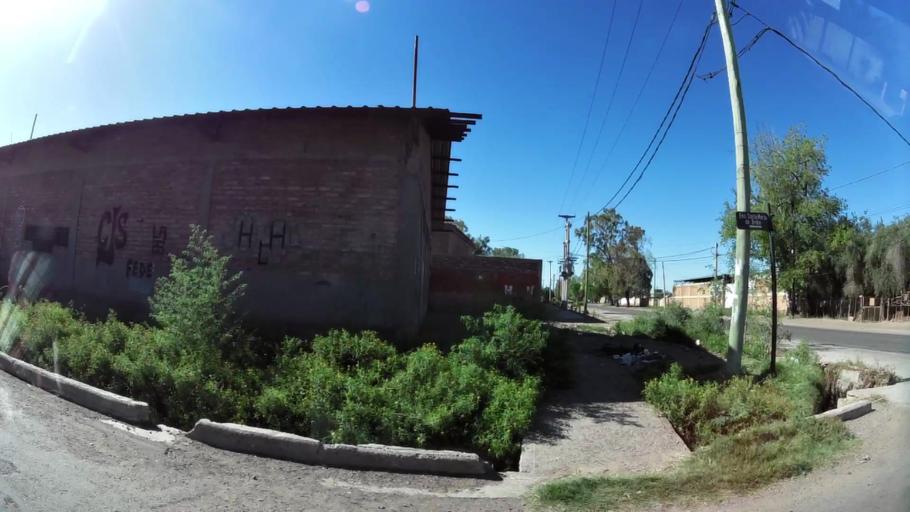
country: AR
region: Mendoza
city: Las Heras
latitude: -32.8363
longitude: -68.8102
